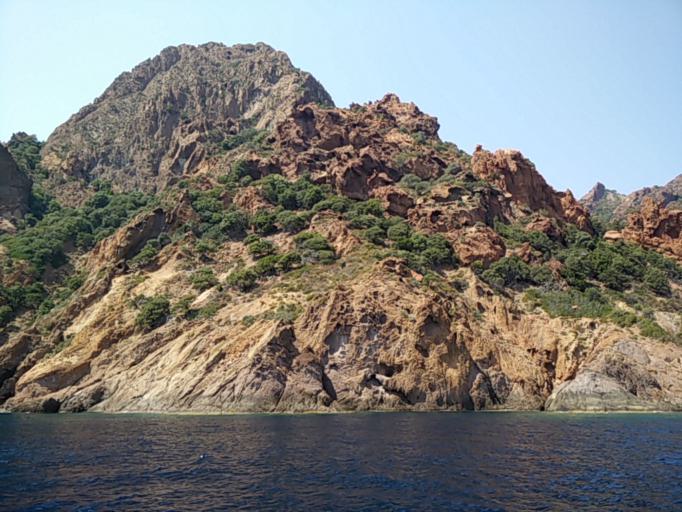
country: FR
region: Corsica
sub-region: Departement de la Corse-du-Sud
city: Cargese
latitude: 42.3383
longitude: 8.5748
